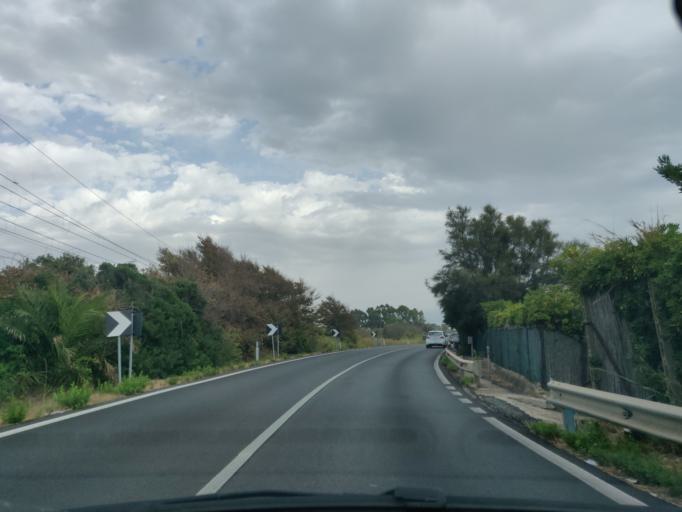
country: IT
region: Latium
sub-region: Citta metropolitana di Roma Capitale
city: Santa Marinella
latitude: 42.0398
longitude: 11.9157
